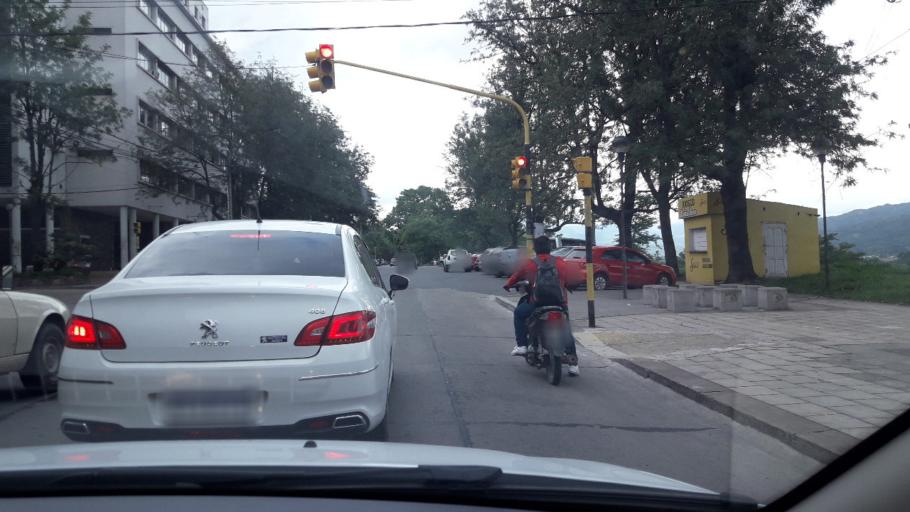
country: AR
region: Jujuy
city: San Salvador de Jujuy
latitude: -24.1799
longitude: -65.3143
